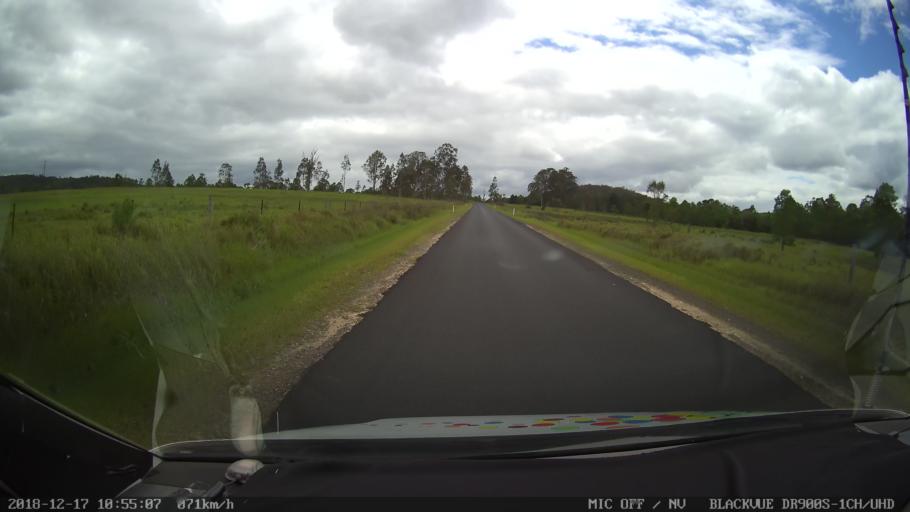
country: AU
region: New South Wales
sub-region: Tenterfield Municipality
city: Carrolls Creek
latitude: -28.8278
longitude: 152.5753
